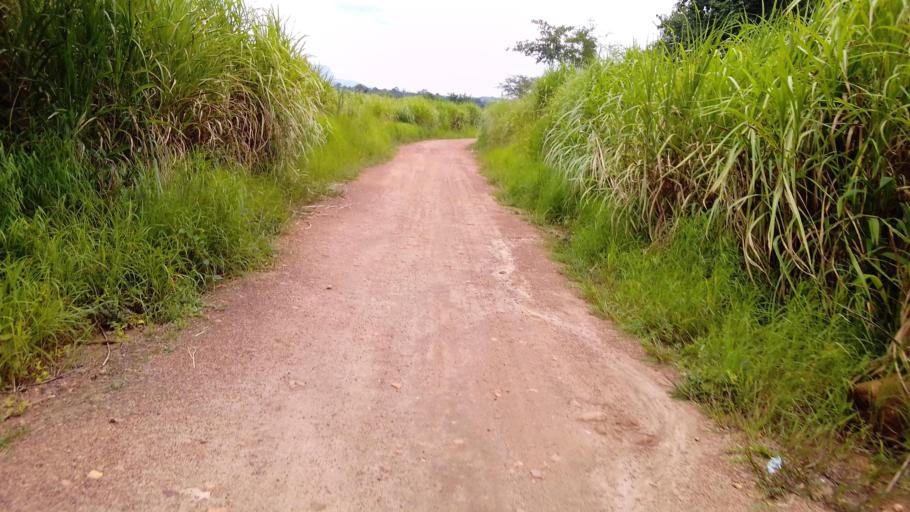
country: SL
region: Eastern Province
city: Koidu
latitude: 8.6847
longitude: -10.9321
